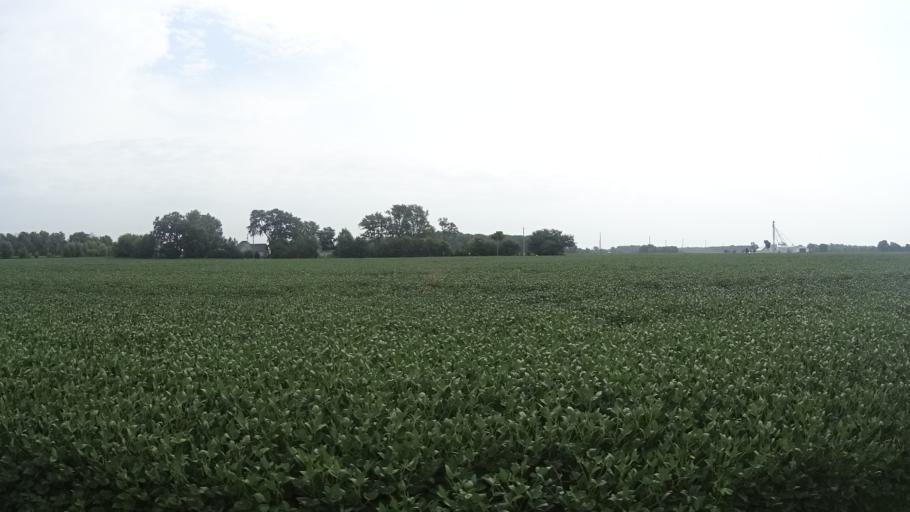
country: US
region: Indiana
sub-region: Madison County
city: Pendleton
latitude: 40.0316
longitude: -85.7915
